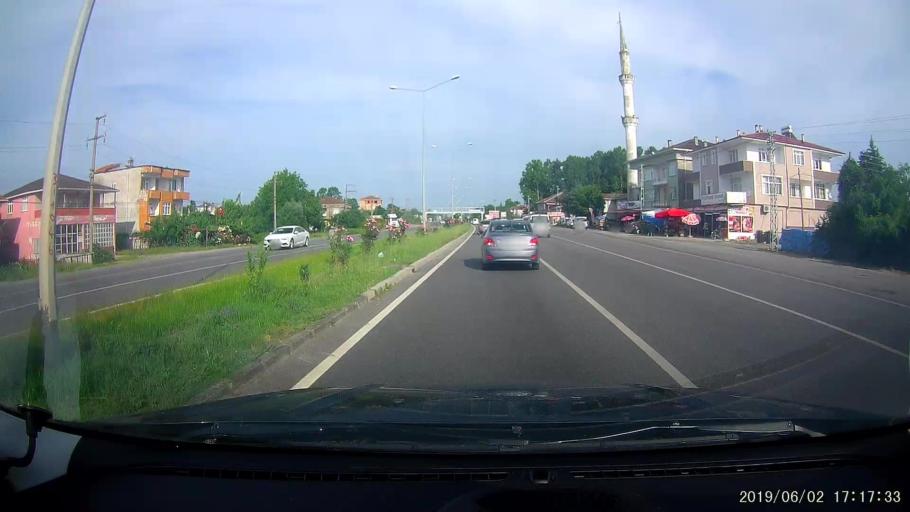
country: TR
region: Samsun
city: Dikbiyik
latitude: 41.2278
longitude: 36.5840
